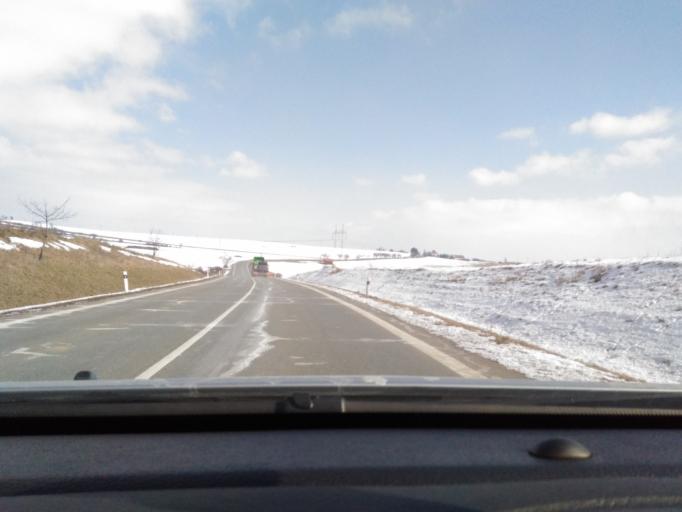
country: CZ
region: Vysocina
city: Krizanov
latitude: 49.3132
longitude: 16.1241
